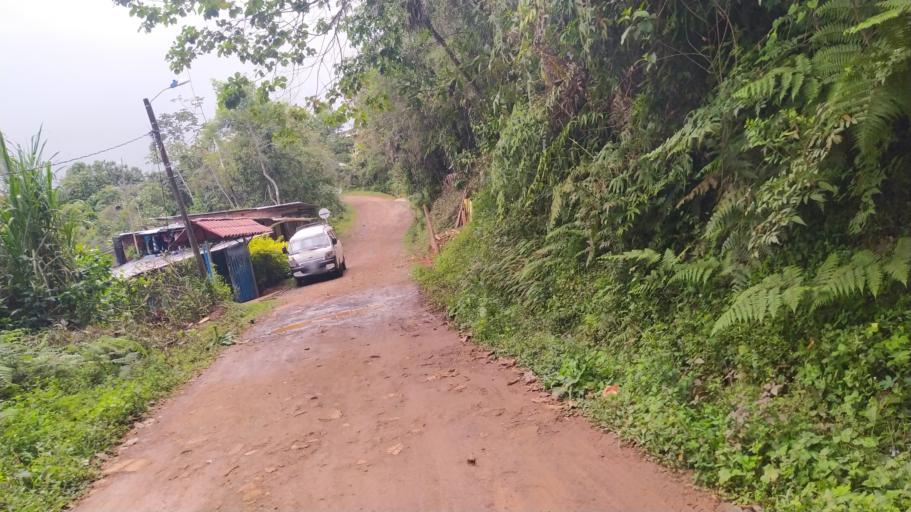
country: CO
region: Valle del Cauca
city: Cali
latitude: 3.4252
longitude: -76.6173
